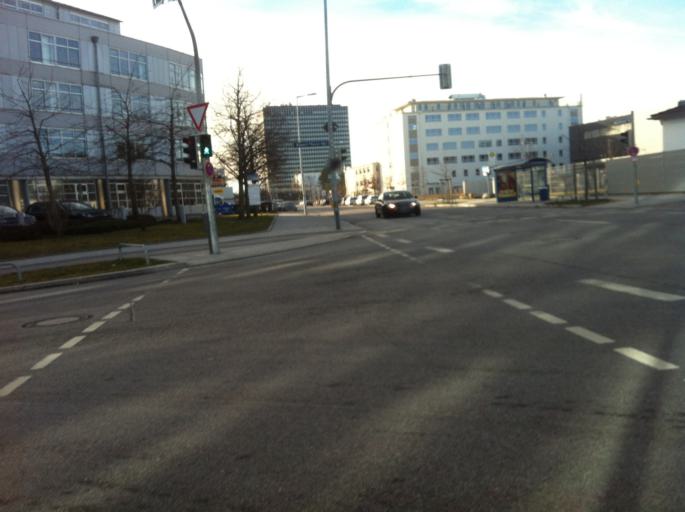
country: DE
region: Bavaria
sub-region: Upper Bavaria
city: Pullach im Isartal
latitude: 48.0956
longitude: 11.5319
